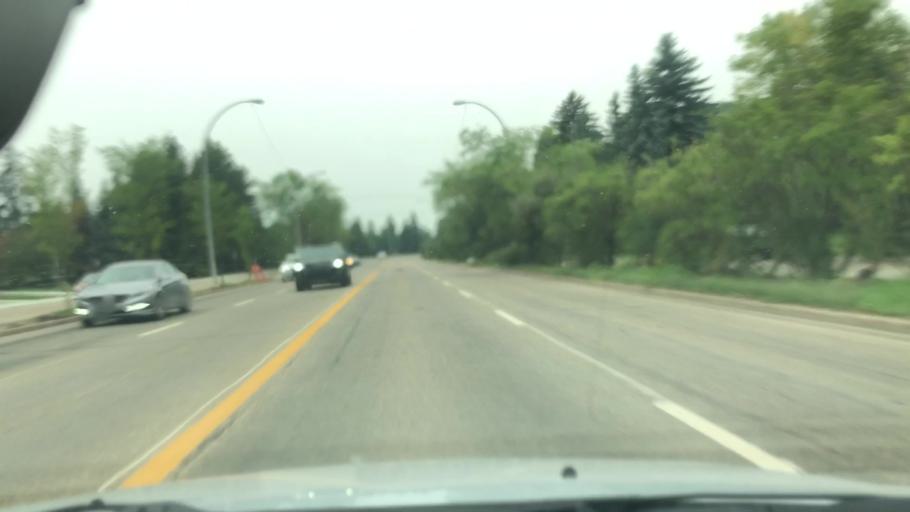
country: CA
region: Alberta
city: Edmonton
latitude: 53.5178
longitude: -113.5333
